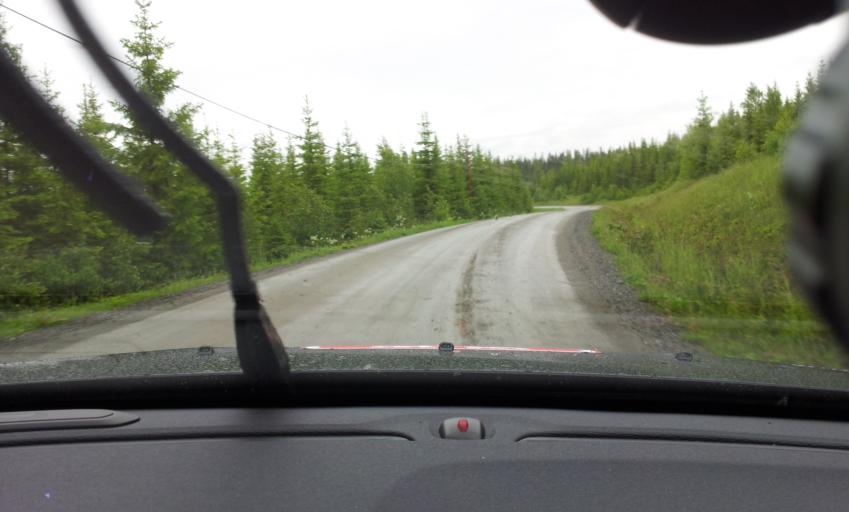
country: SE
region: Jaemtland
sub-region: Are Kommun
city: Are
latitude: 63.4217
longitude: 12.8207
